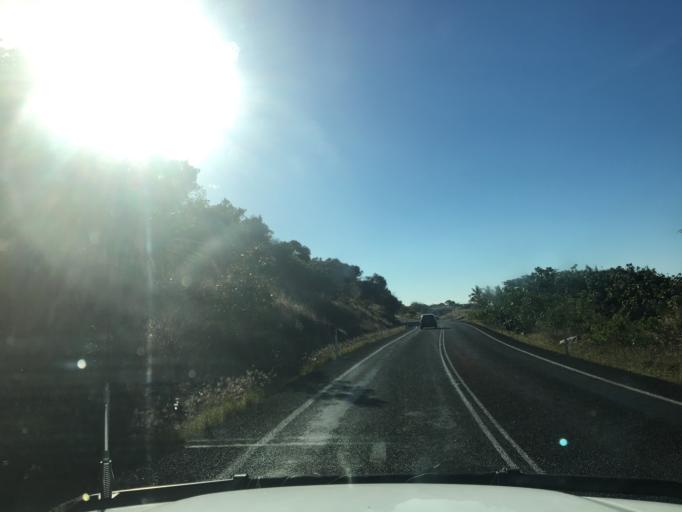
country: AU
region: Queensland
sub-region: Cairns
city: Palm Cove
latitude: -16.7155
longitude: 145.6368
